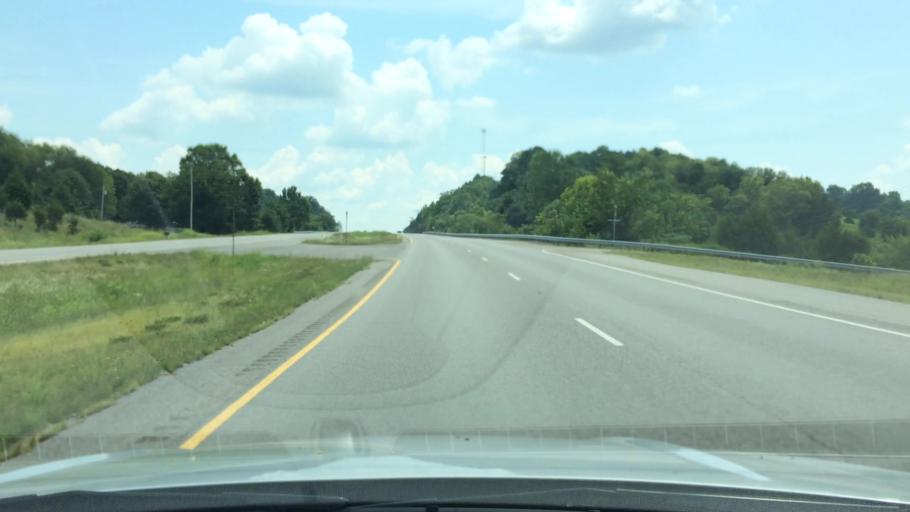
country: US
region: Tennessee
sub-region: Giles County
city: Pulaski
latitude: 35.1774
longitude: -86.9555
